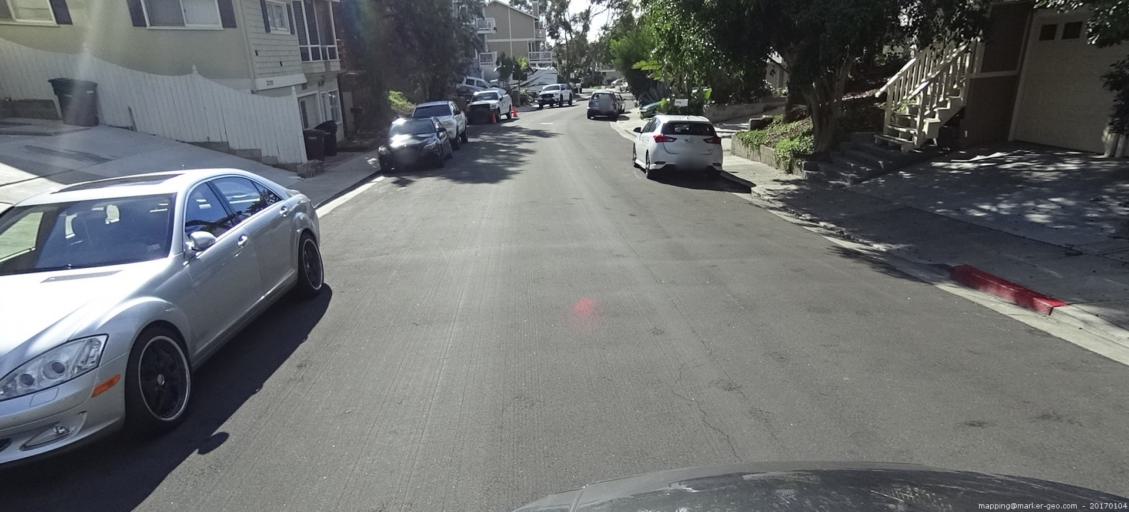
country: US
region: California
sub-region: Orange County
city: Dana Point
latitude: 33.4722
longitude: -117.6995
